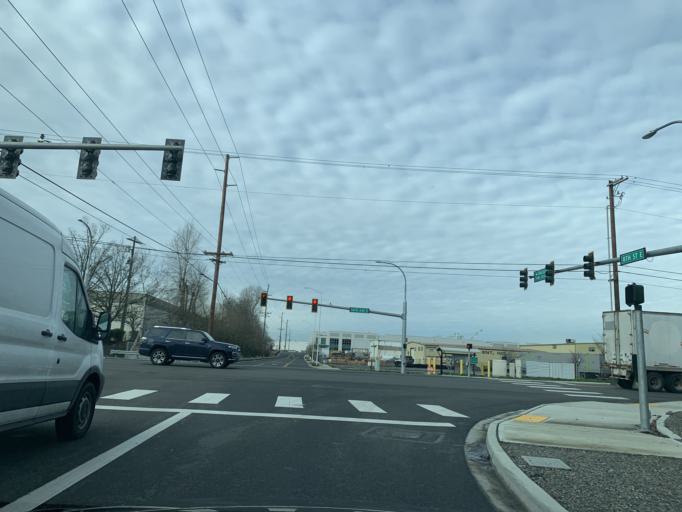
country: US
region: Washington
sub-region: Pierce County
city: Fife
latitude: 47.2500
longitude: -122.3564
